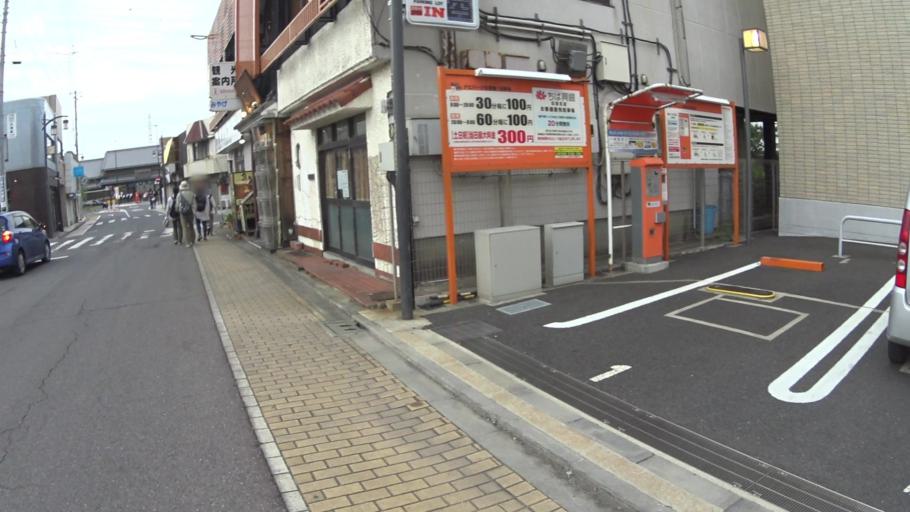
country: JP
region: Chiba
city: Katori-shi
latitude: 35.8937
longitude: 140.4933
